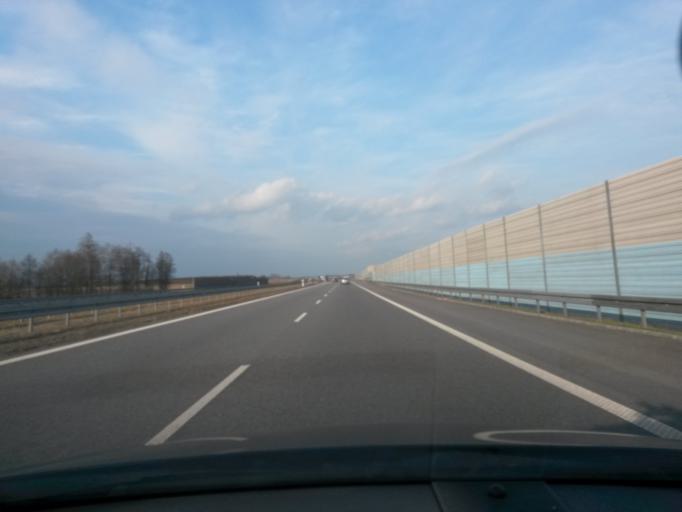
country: PL
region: Lodz Voivodeship
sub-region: Powiat brzezinski
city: Dmosin
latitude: 51.9377
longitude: 19.8144
